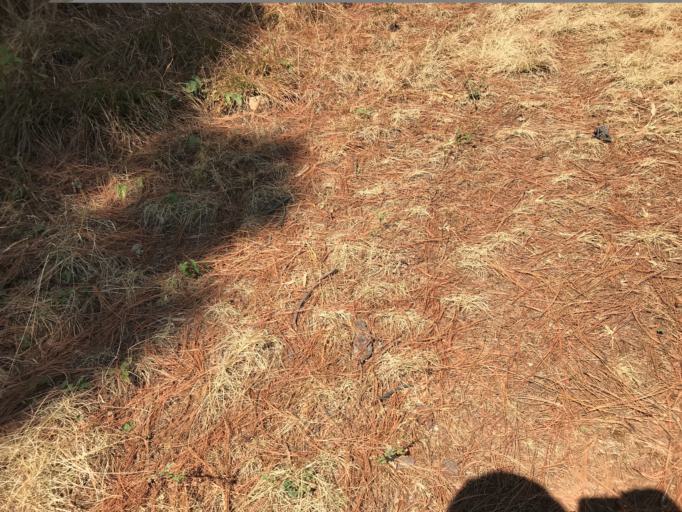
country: GT
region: Guatemala
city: Villa Canales
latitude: 14.4803
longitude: -90.5444
